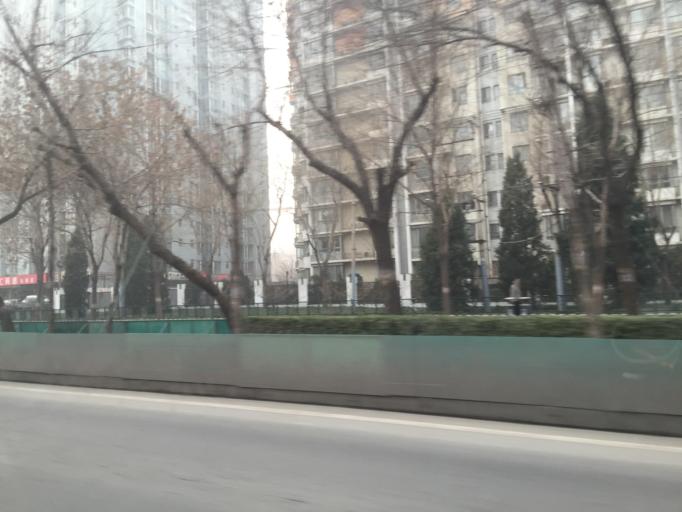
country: CN
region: Beijing
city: Qinghe
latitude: 40.0117
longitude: 116.3460
